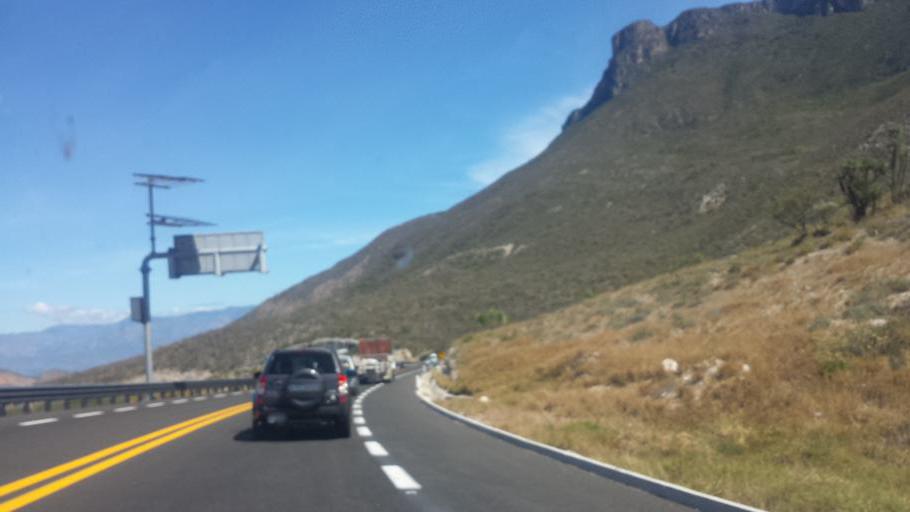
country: MX
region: Puebla
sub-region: San Jose Miahuatlan
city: San Pedro Tetitlan
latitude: 18.1237
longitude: -97.3360
